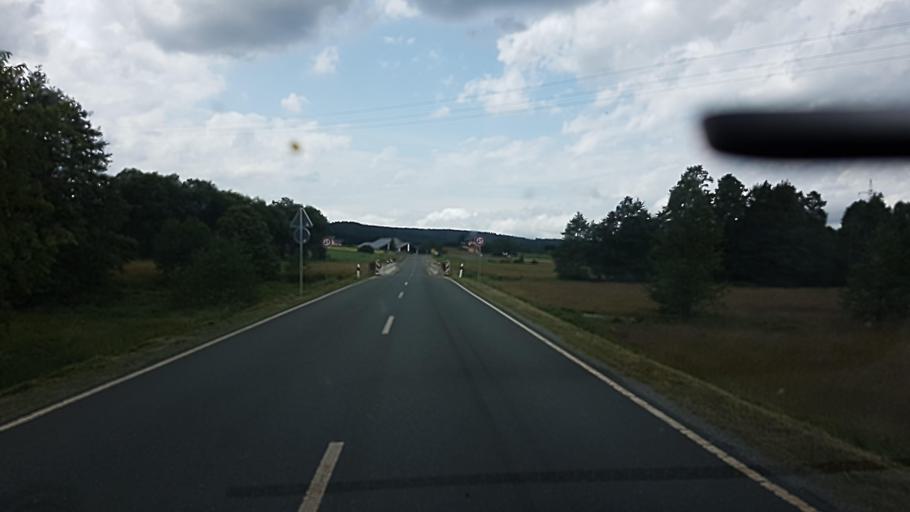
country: DE
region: Bavaria
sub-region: Upper Franconia
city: Mehlmeisel
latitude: 49.9828
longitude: 11.8643
